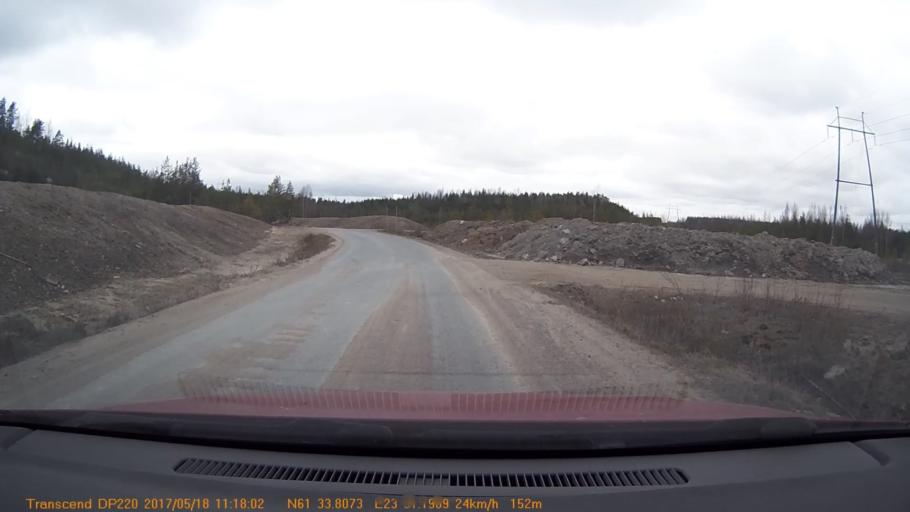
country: FI
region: Pirkanmaa
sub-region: Tampere
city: Yloejaervi
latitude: 61.5634
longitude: 23.5199
